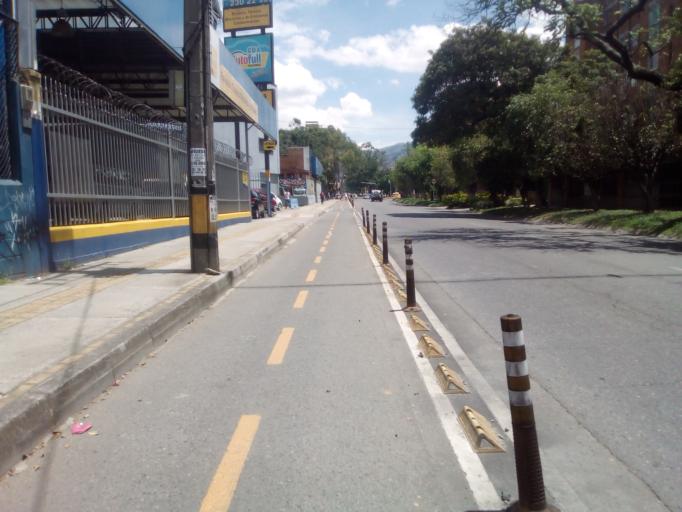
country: CO
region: Antioquia
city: Medellin
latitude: 6.2568
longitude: -75.5818
